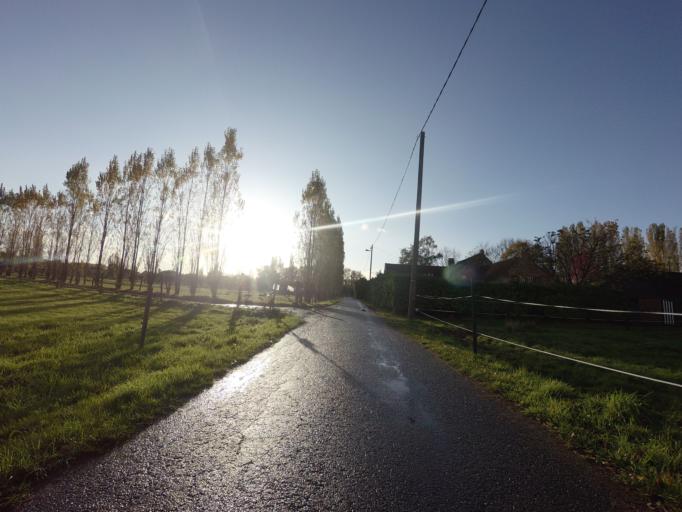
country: BE
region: Flanders
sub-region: Provincie Antwerpen
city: Schelle
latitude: 51.1266
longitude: 4.3616
